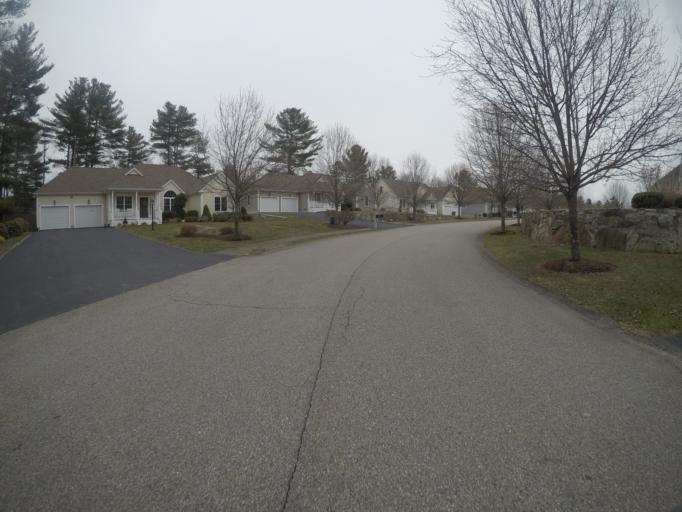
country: US
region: Massachusetts
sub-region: Bristol County
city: Easton
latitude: 42.0322
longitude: -71.1538
